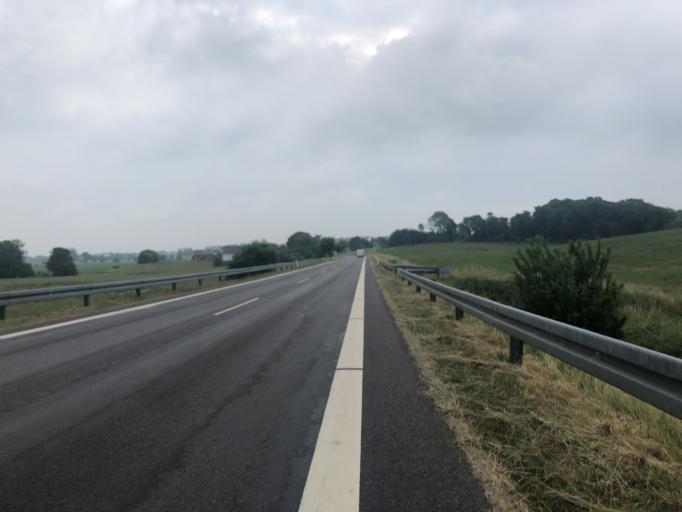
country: DK
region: Capital Region
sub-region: Bornholm Kommune
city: Akirkeby
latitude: 55.1523
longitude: 14.8987
